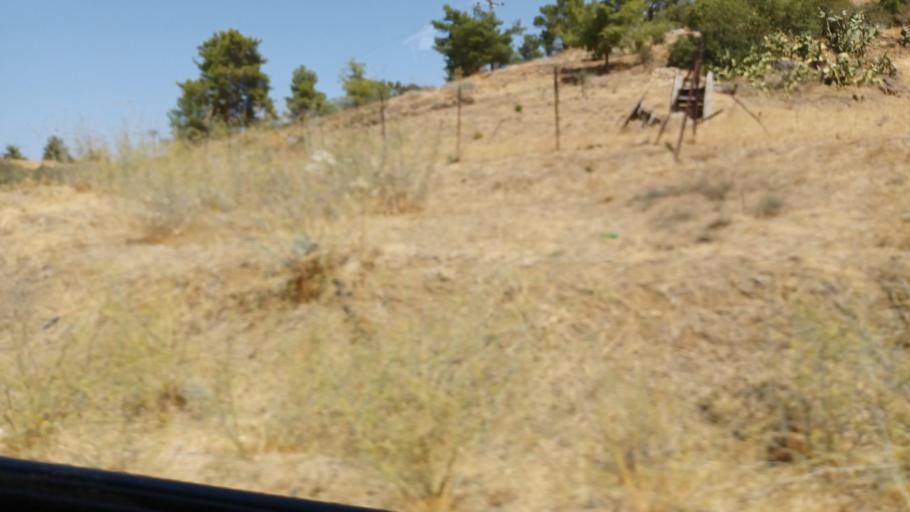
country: CY
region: Lefkosia
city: Kakopetria
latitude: 35.0499
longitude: 32.8949
